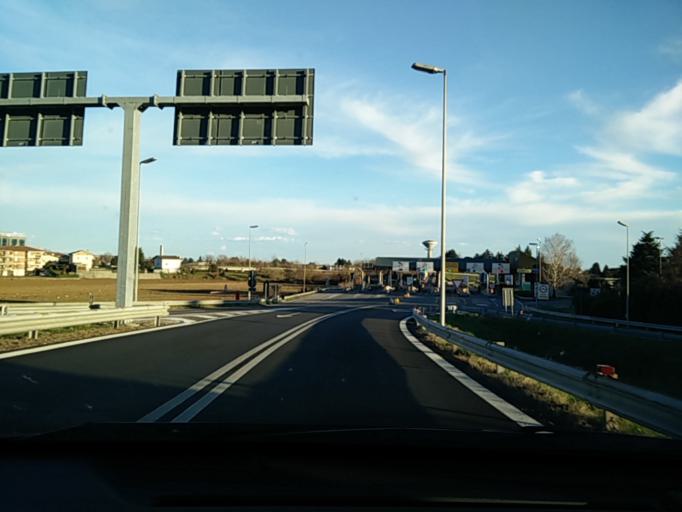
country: IT
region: Friuli Venezia Giulia
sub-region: Provincia di Udine
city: Tavagnacco
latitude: 46.1133
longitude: 13.2064
